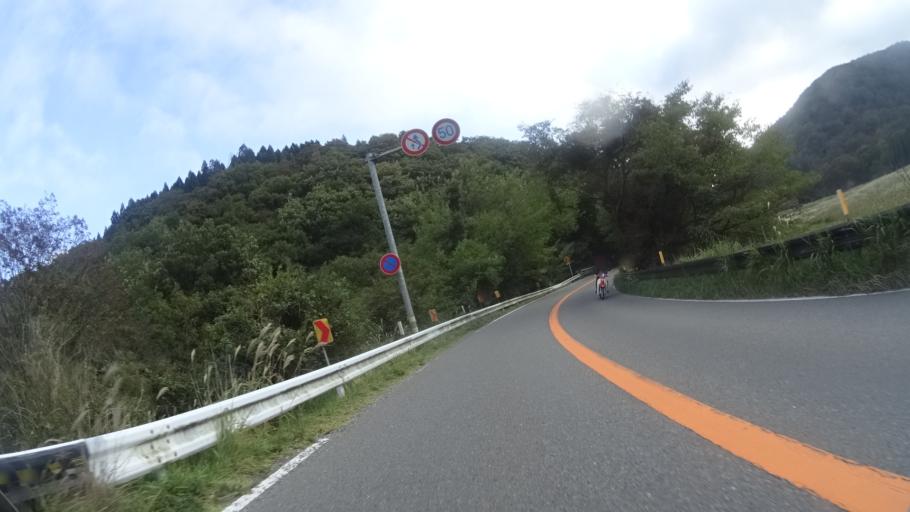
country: JP
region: Oita
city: Beppu
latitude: 33.2736
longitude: 131.4162
